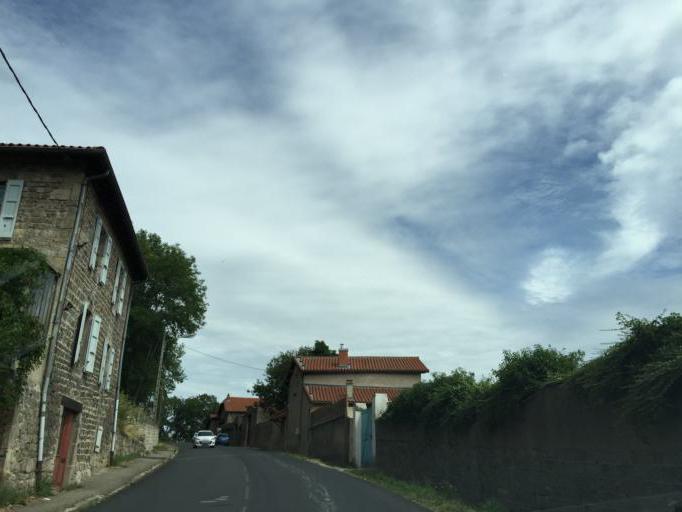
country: FR
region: Rhone-Alpes
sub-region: Departement de la Loire
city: Saint-Bonnet-le-Chateau
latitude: 45.4233
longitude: 4.0688
